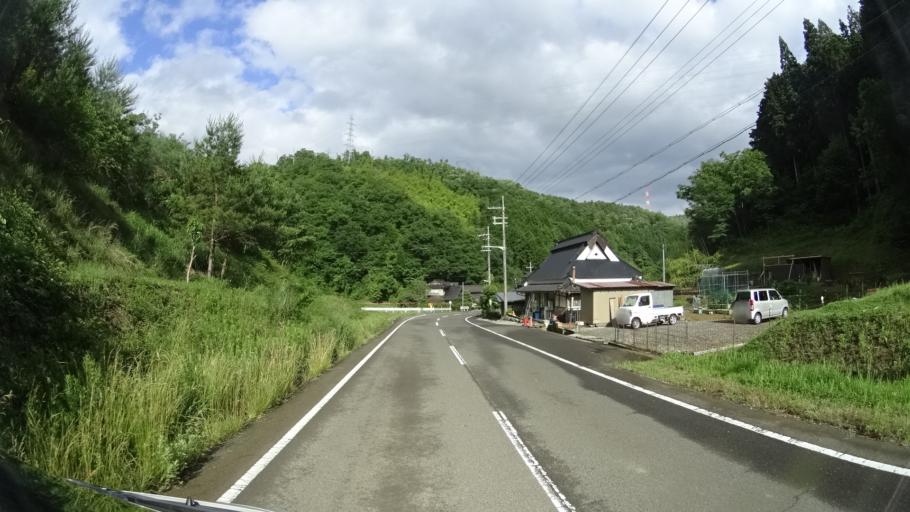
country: JP
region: Kyoto
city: Ayabe
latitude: 35.3713
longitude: 135.2861
